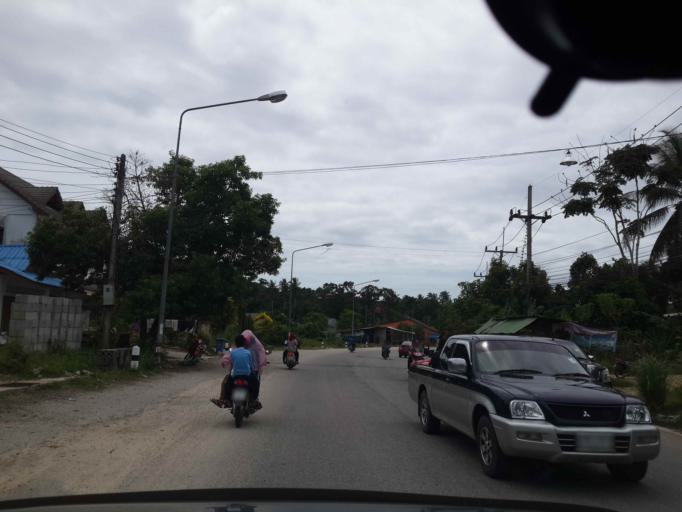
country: TH
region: Narathiwat
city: Yi-ngo
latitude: 6.3370
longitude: 101.6372
